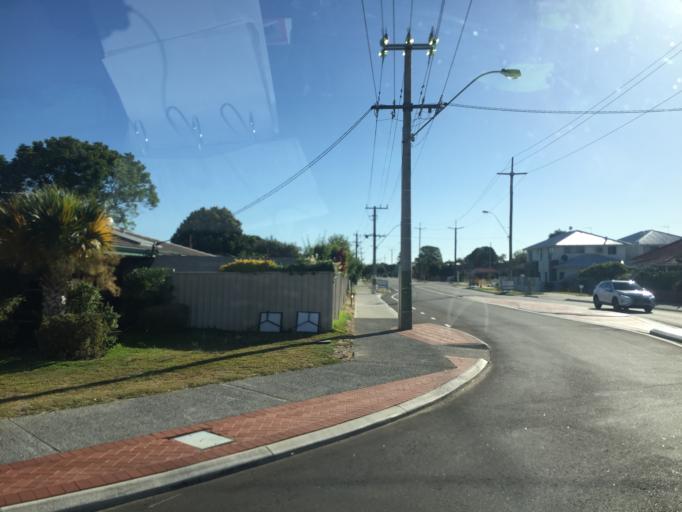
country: AU
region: Western Australia
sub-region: Belmont
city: Rivervale
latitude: -31.9613
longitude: 115.9282
